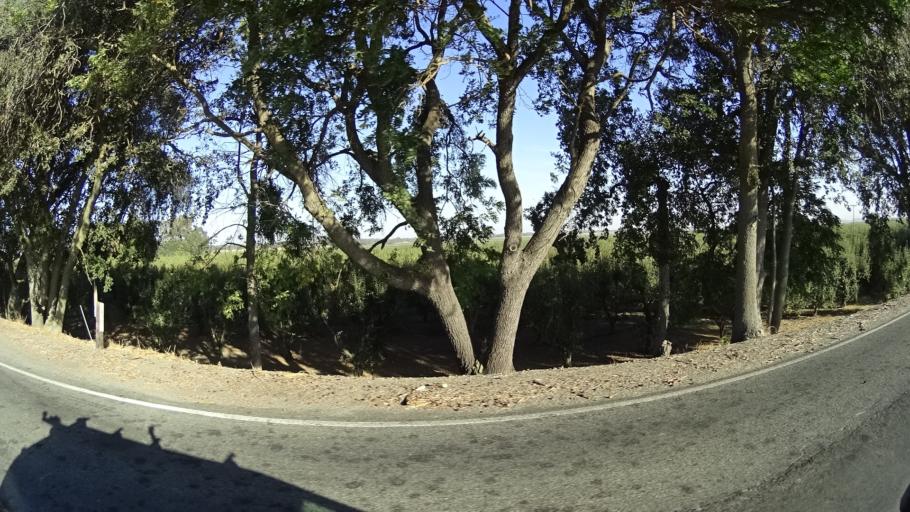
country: US
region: California
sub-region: Sacramento County
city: Walnut Grove
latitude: 38.3454
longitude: -121.5556
